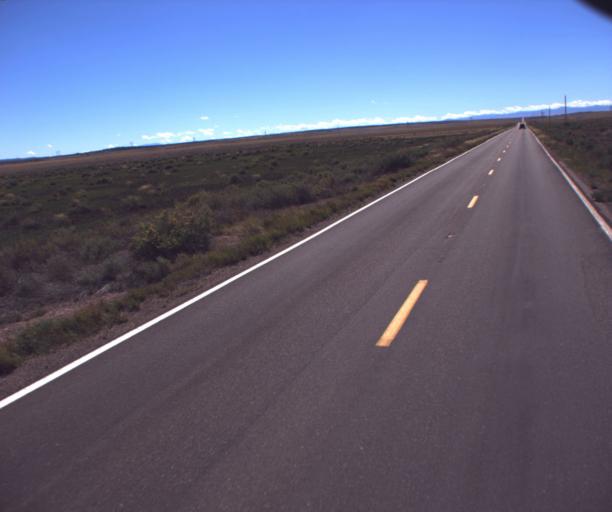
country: US
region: Arizona
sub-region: Apache County
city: Saint Johns
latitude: 34.6132
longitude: -109.3192
